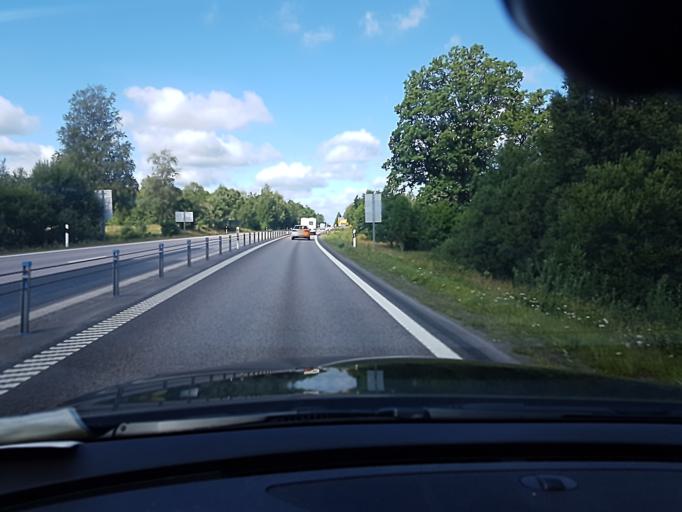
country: SE
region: Kalmar
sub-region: Nybro Kommun
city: Nybro
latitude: 56.7270
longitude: 15.9847
